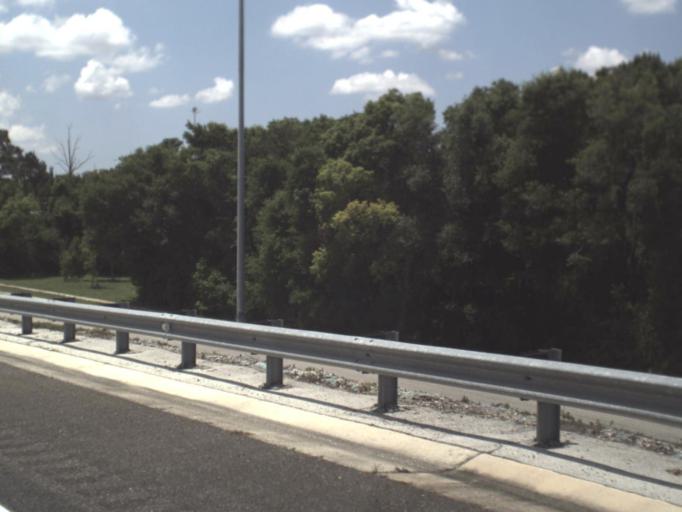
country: US
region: Florida
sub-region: Duval County
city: Jacksonville
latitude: 30.3515
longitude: -81.5526
